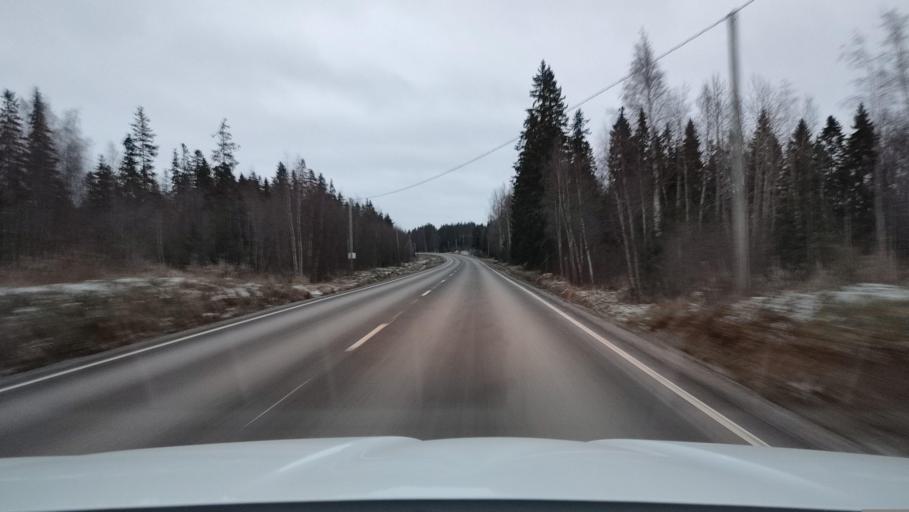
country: FI
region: Ostrobothnia
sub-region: Vaasa
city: Replot
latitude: 63.2135
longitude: 21.4296
